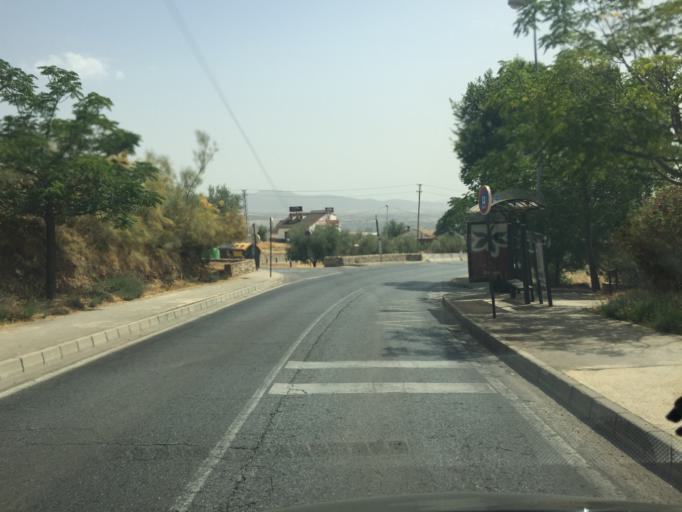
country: ES
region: Andalusia
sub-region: Provincia de Granada
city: Huetor Vega
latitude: 37.1702
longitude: -3.5817
